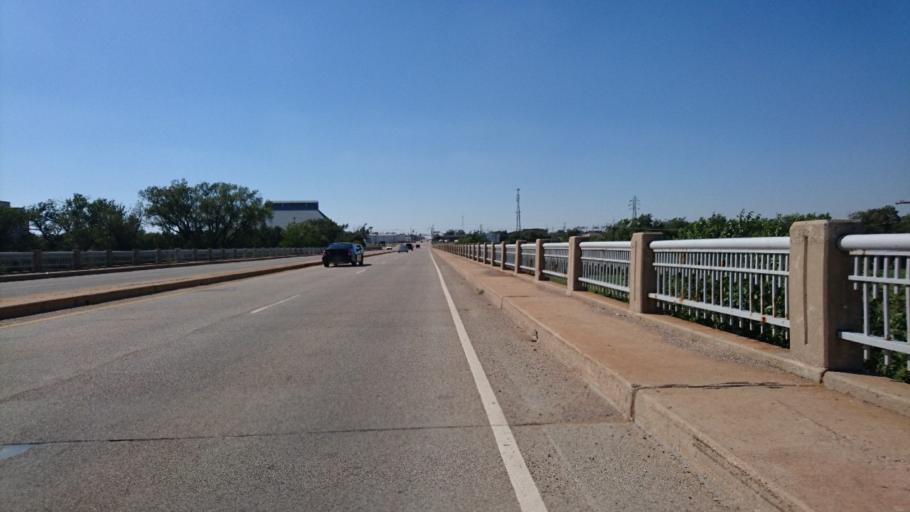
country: US
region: Oklahoma
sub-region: Custer County
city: Clinton
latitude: 35.5156
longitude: -98.9555
